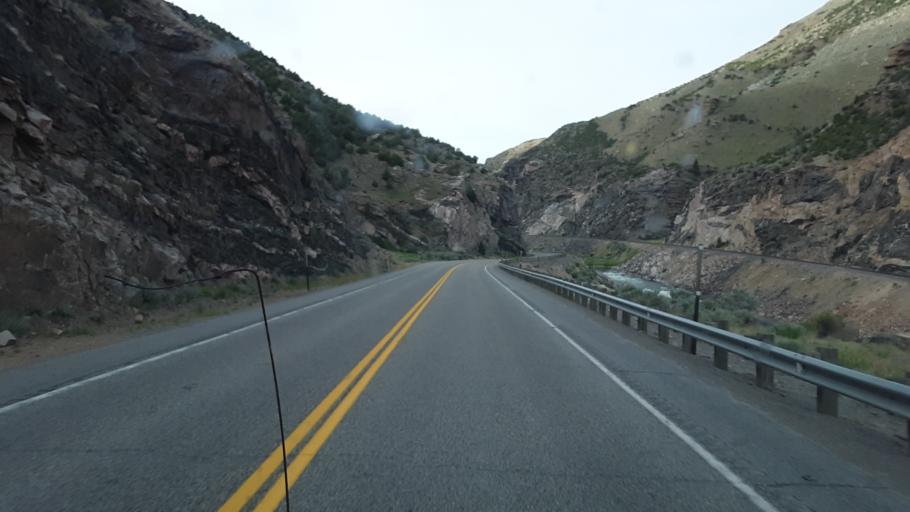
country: US
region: Wyoming
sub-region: Hot Springs County
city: Thermopolis
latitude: 43.4628
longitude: -108.1705
